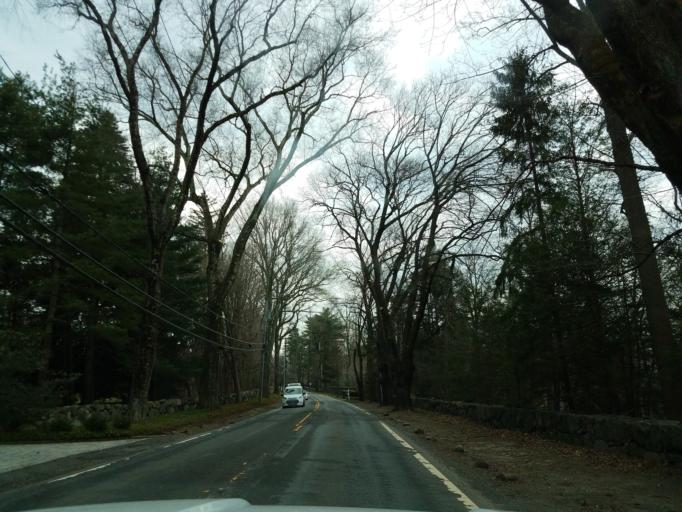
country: US
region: Connecticut
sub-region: Fairfield County
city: Glenville
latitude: 41.0559
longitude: -73.6394
